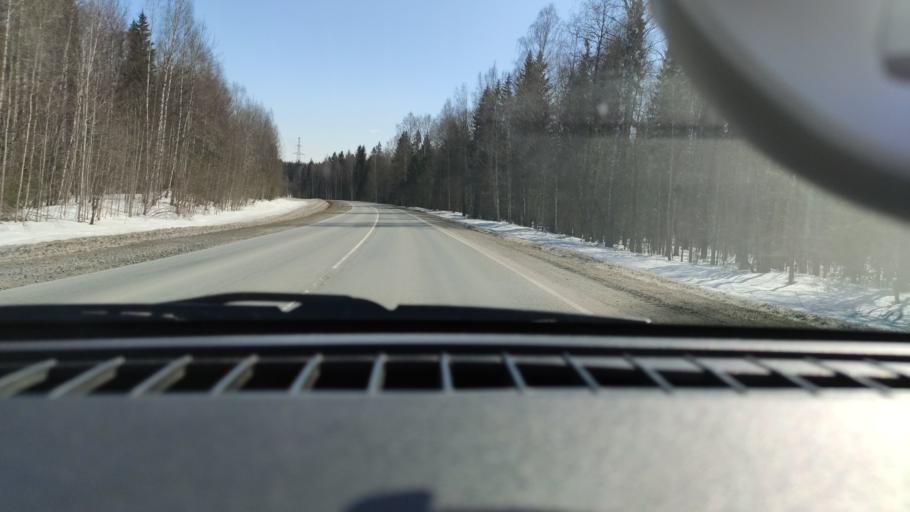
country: RU
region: Perm
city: Perm
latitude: 58.1418
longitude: 56.2669
